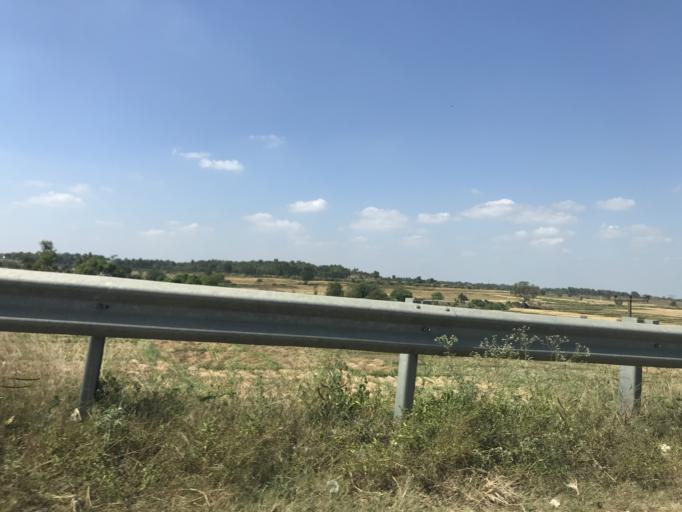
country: IN
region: Karnataka
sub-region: Mysore
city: Hunsur
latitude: 12.4512
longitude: 76.3858
